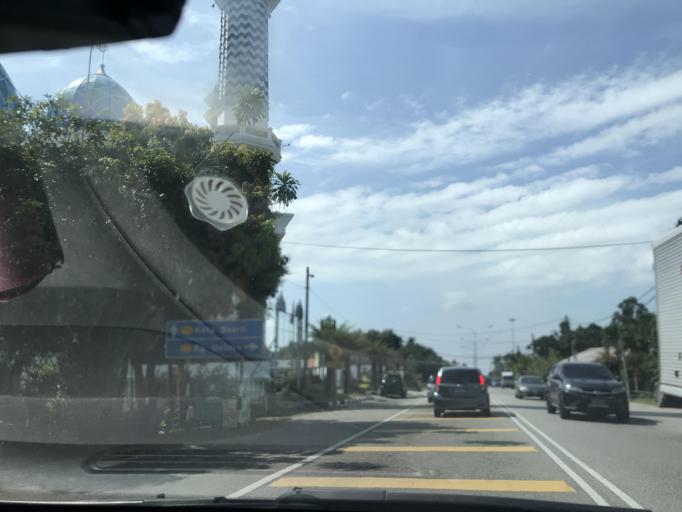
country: MY
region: Kelantan
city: Kota Bharu
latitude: 6.1329
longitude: 102.1759
